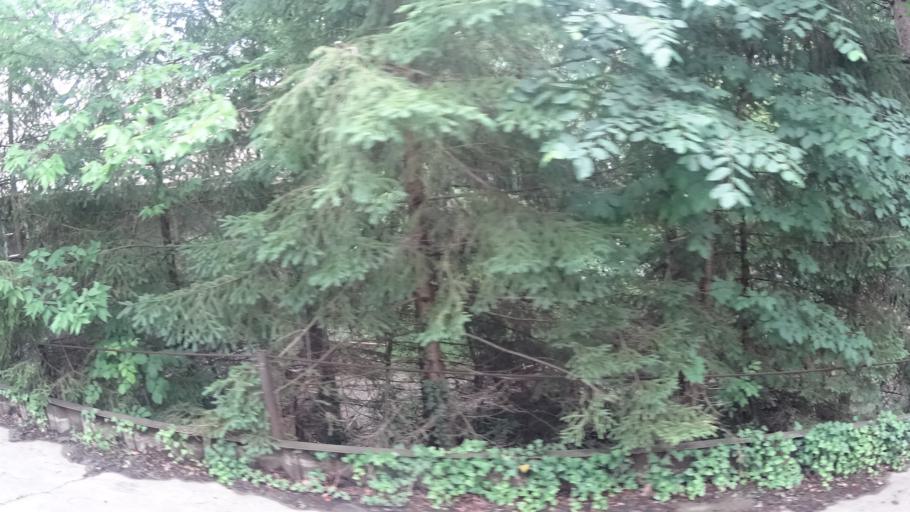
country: US
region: Ohio
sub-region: Erie County
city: Milan
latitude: 41.3431
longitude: -82.5757
